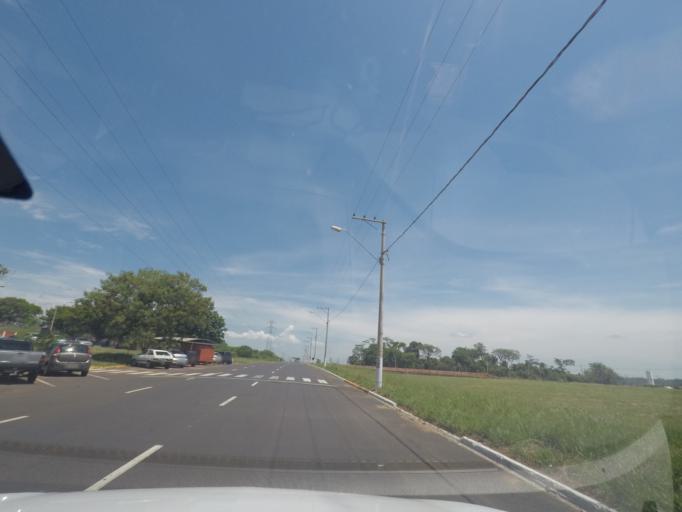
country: BR
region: Sao Paulo
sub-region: Matao
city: Matao
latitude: -21.6108
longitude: -48.3761
